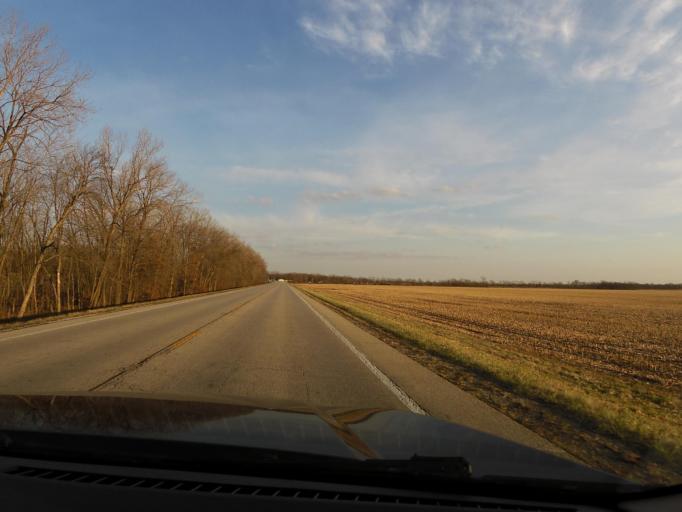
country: US
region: Illinois
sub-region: Fayette County
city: Vandalia
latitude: 38.9512
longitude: -89.0850
